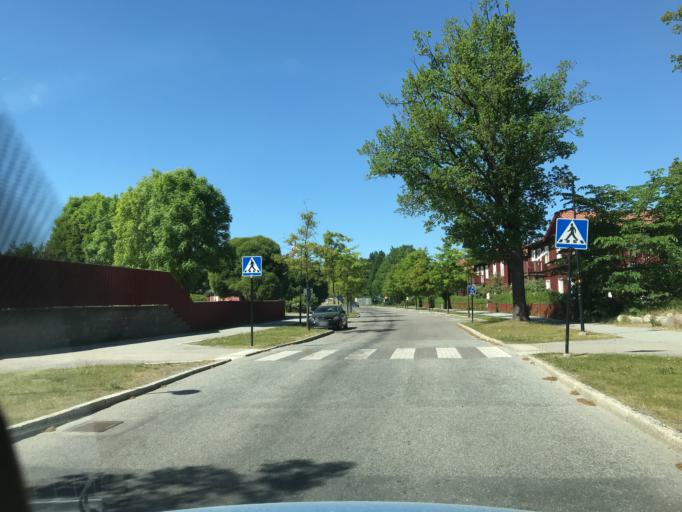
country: SE
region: Stockholm
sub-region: Stockholms Kommun
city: Kista
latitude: 59.4039
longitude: 17.9798
